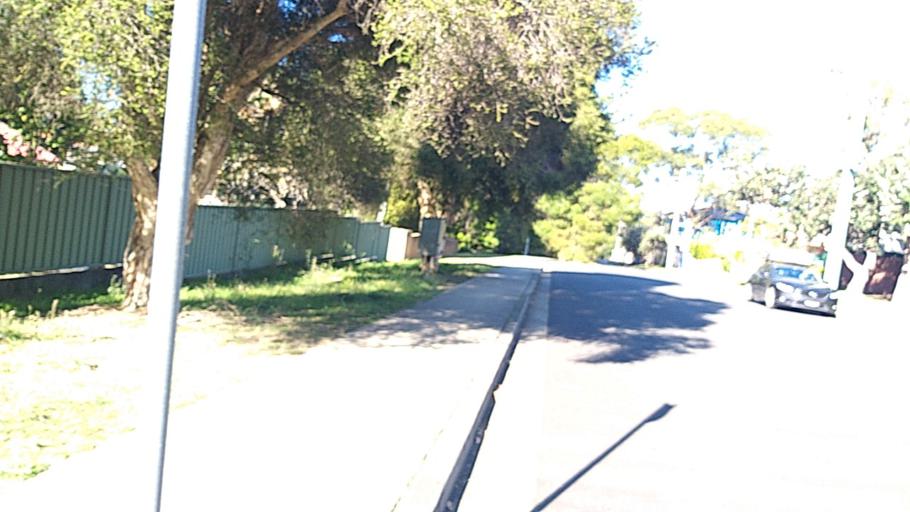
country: AU
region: New South Wales
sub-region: Ryde
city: East Ryde
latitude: -33.8228
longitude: 151.1175
